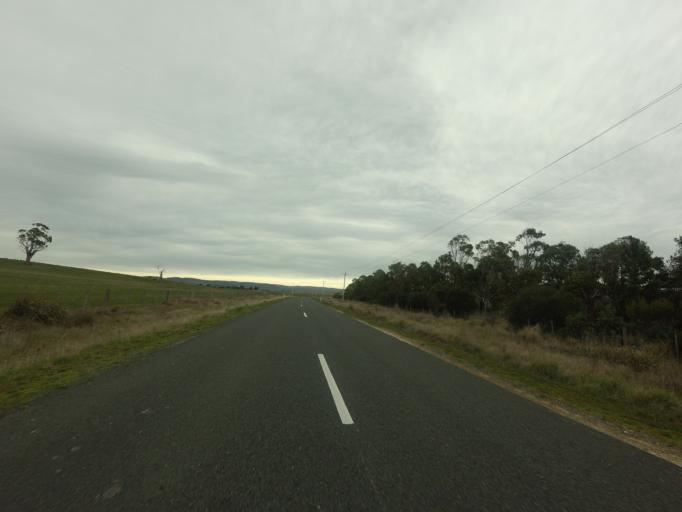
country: AU
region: Tasmania
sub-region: Derwent Valley
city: New Norfolk
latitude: -42.4110
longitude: 147.0075
